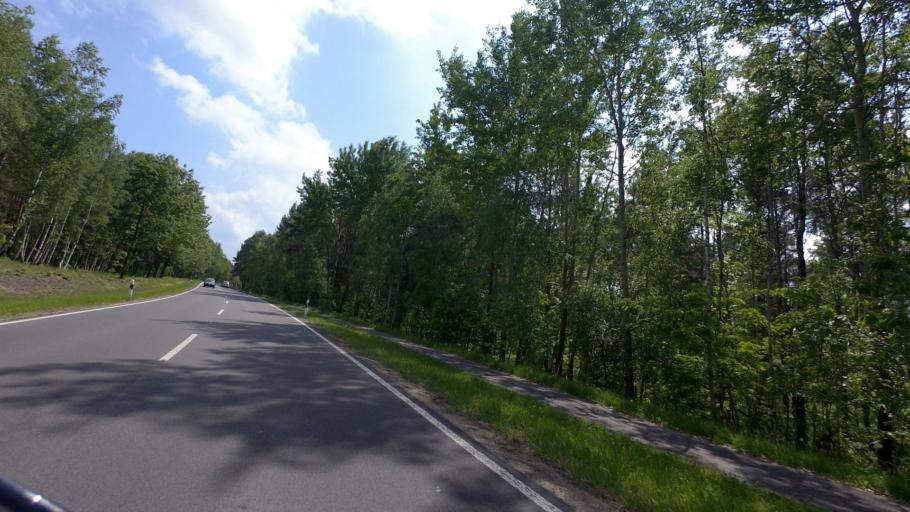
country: DE
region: Saxony
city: Trebendorf
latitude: 51.5280
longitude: 14.6010
